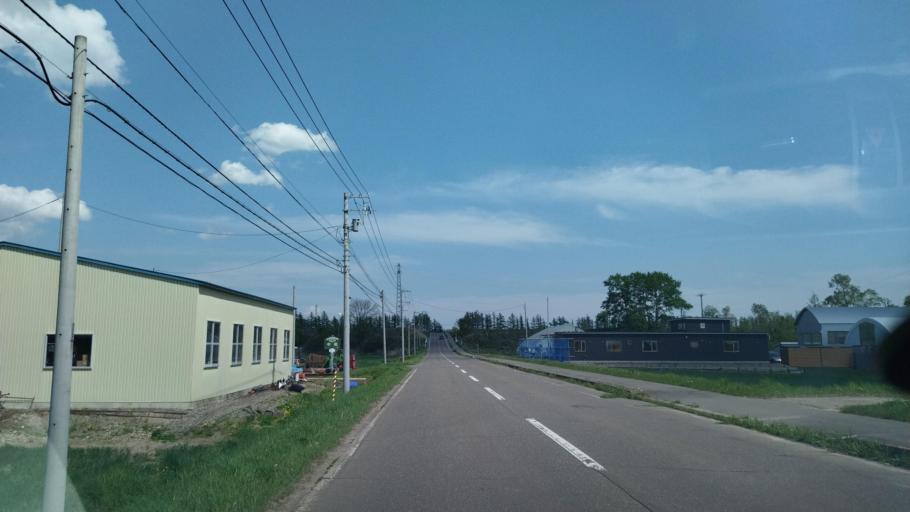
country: JP
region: Hokkaido
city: Otofuke
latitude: 43.1013
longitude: 143.2179
